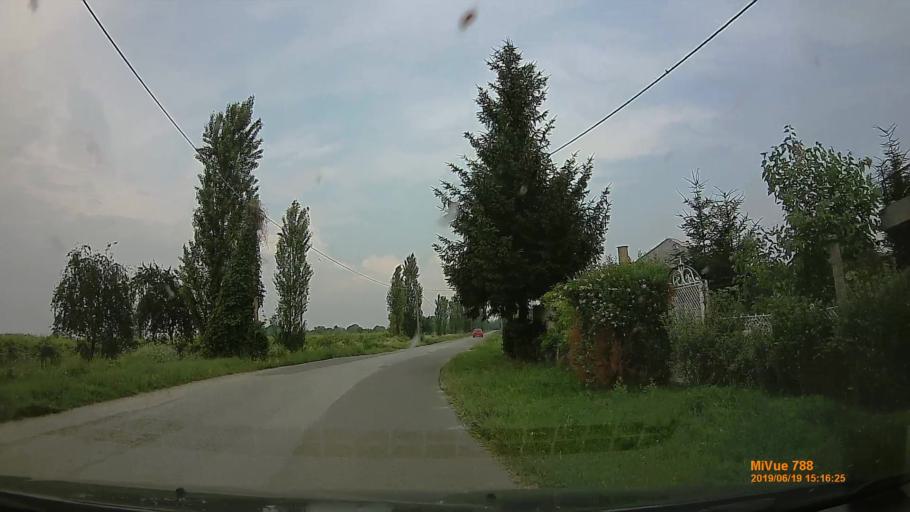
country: HU
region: Baranya
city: Szigetvar
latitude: 46.0774
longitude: 17.8407
